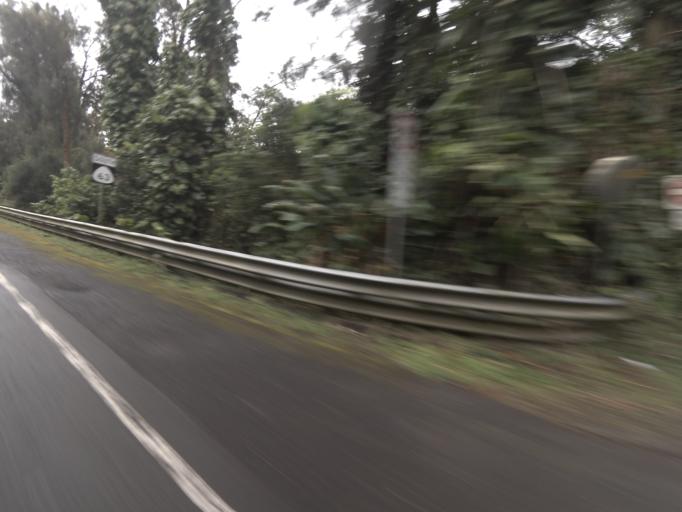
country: US
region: Hawaii
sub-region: Honolulu County
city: Kane'ohe
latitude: 21.3747
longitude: -157.8215
